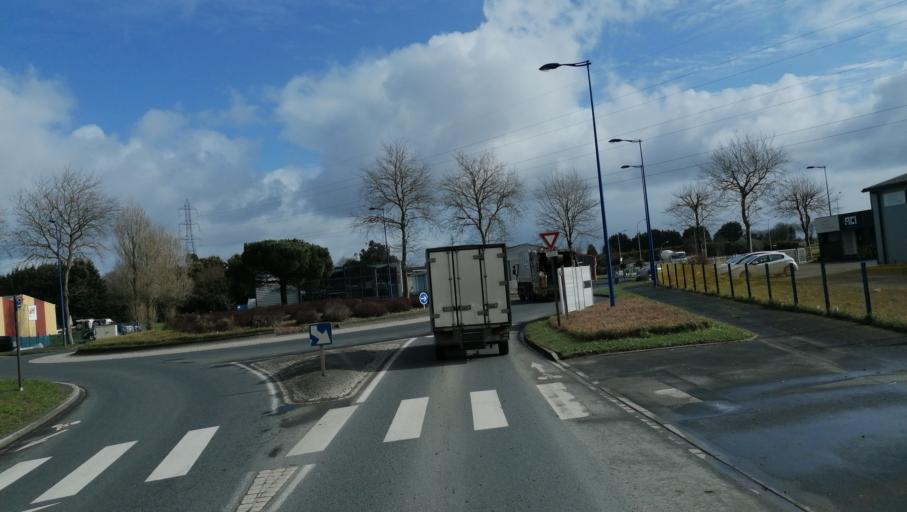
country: FR
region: Brittany
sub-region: Departement des Cotes-d'Armor
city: Saint-Julien
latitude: 48.4617
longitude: -2.7857
